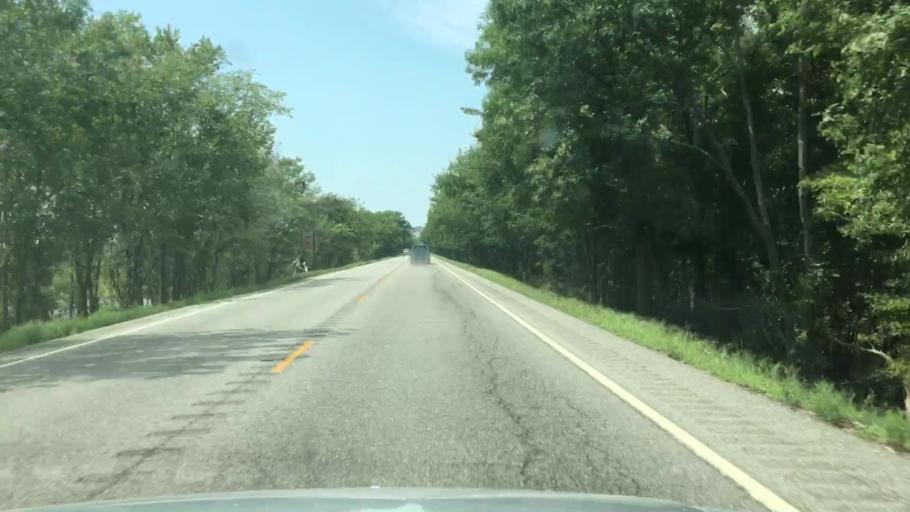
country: US
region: Oklahoma
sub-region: Muskogee County
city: Fort Gibson
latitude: 35.9370
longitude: -95.2132
